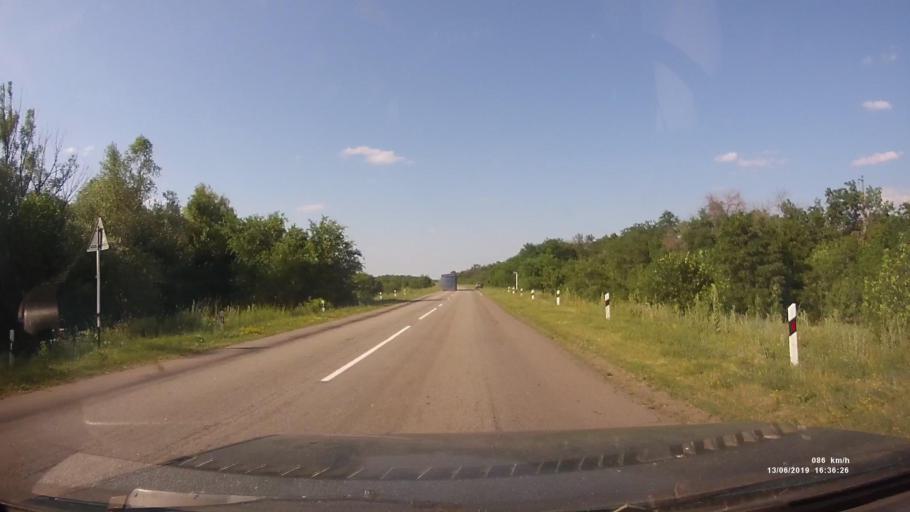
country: RU
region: Rostov
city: Kazanskaya
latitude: 49.8949
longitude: 41.3059
